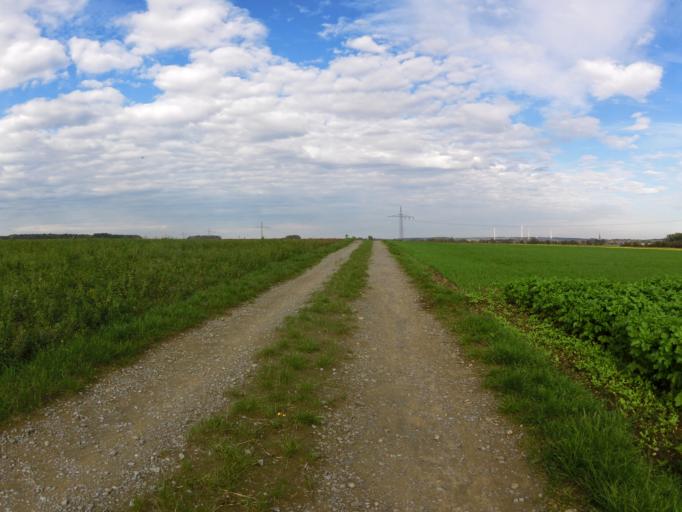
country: DE
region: Bavaria
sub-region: Regierungsbezirk Unterfranken
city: Frickenhausen
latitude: 49.7171
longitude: 10.0780
